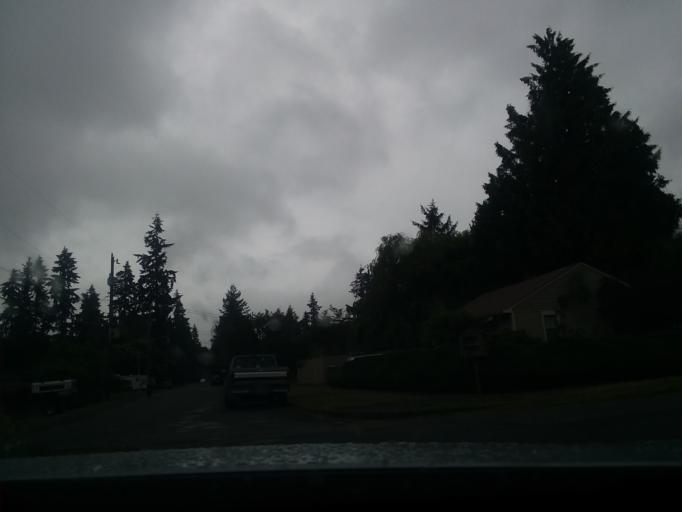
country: US
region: Washington
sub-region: King County
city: Shoreline
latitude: 47.7287
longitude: -122.3396
